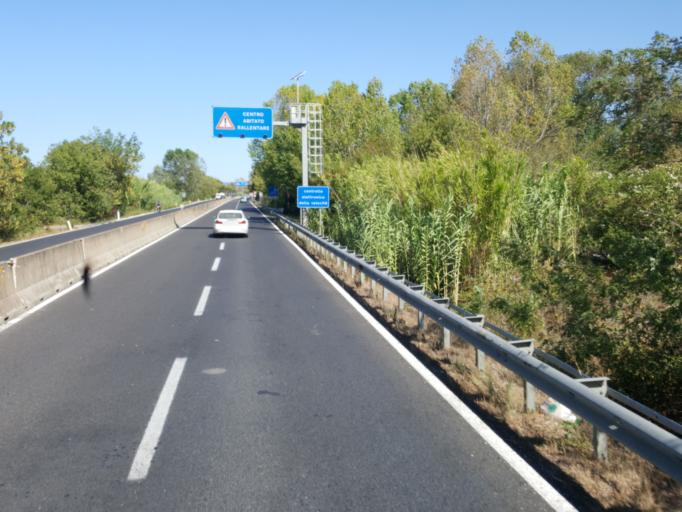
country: IT
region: Tuscany
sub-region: Provincia di Grosseto
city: Albinia
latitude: 42.4899
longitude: 11.2133
